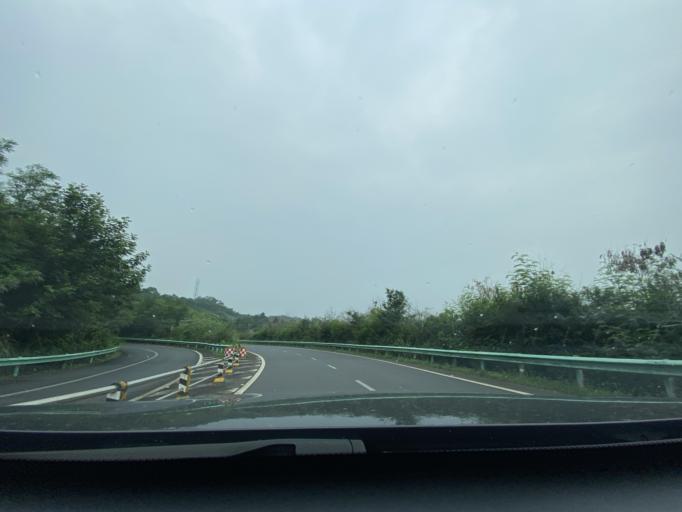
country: CN
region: Sichuan
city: Wenlin
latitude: 30.2970
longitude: 104.1248
